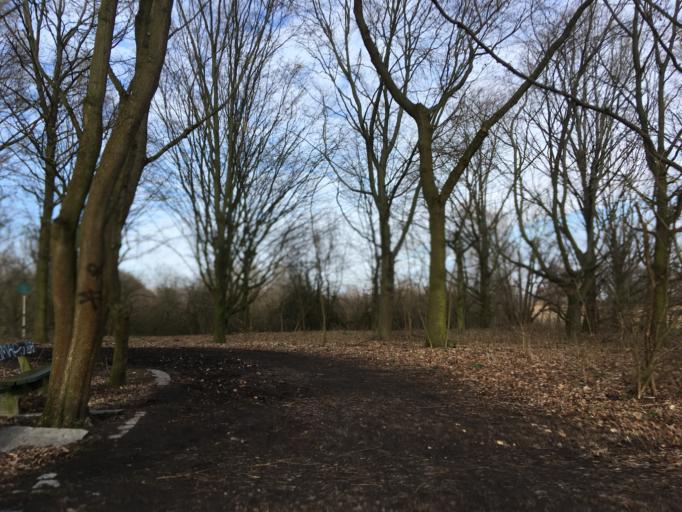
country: DE
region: Berlin
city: Rosenthal
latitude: 52.6084
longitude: 13.3738
